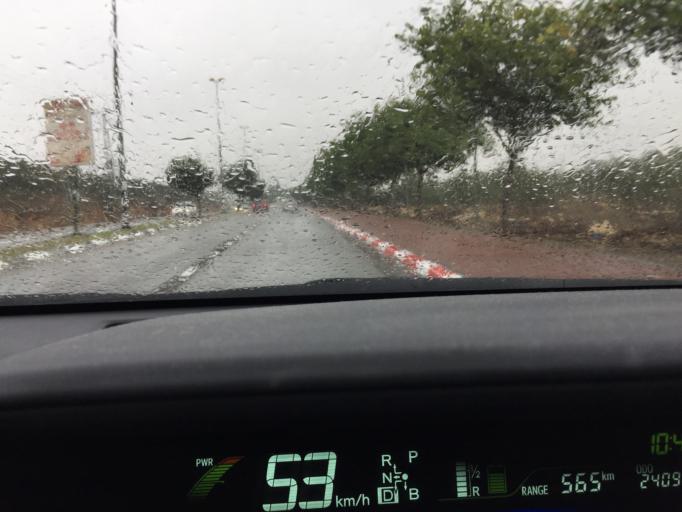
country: PS
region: West Bank
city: Kifil Haris
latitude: 32.1044
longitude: 35.1642
